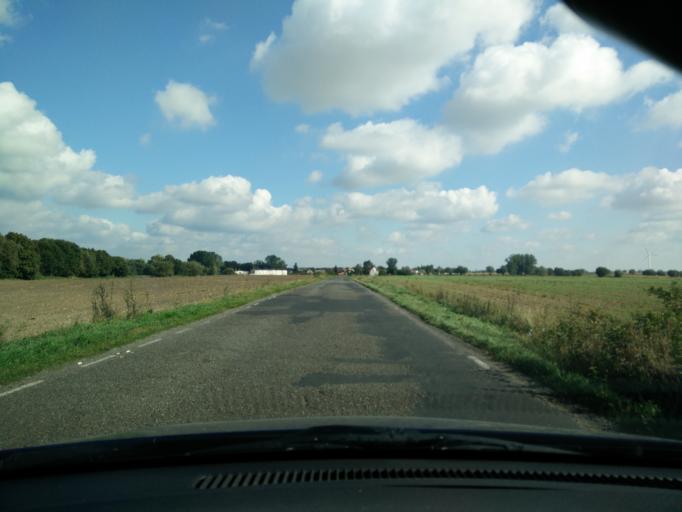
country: PL
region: Greater Poland Voivodeship
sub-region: Powiat sredzki
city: Dominowo
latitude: 52.3137
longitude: 17.3622
